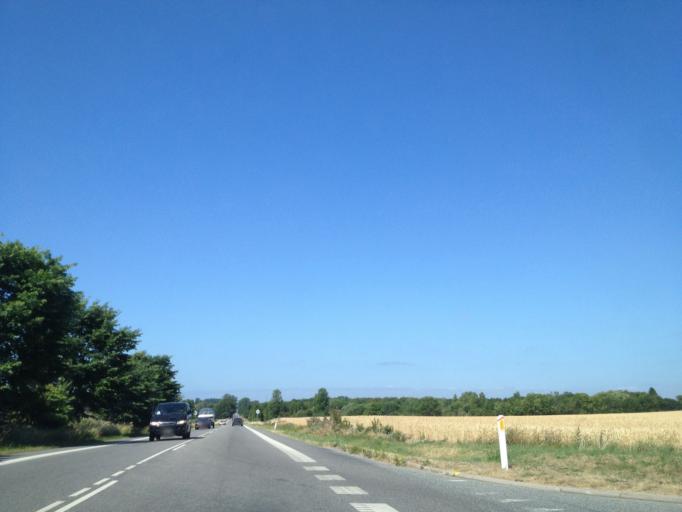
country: DK
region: Capital Region
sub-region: Fredensborg Kommune
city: Niva
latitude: 55.9469
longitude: 12.4898
